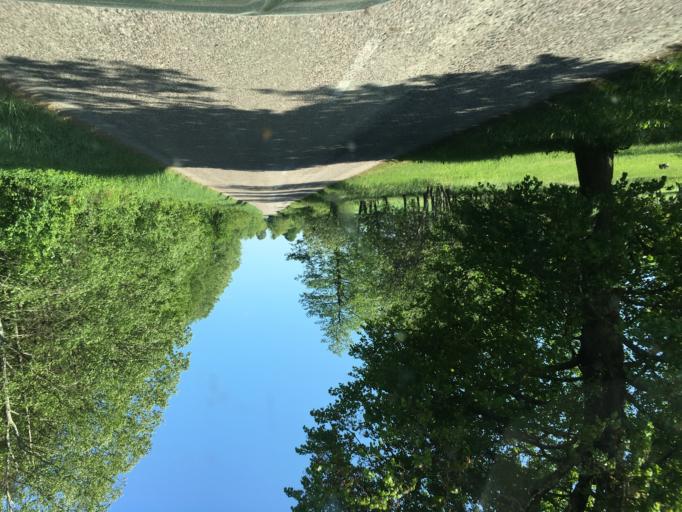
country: LV
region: Ventspils
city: Ventspils
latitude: 57.5035
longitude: 21.8467
